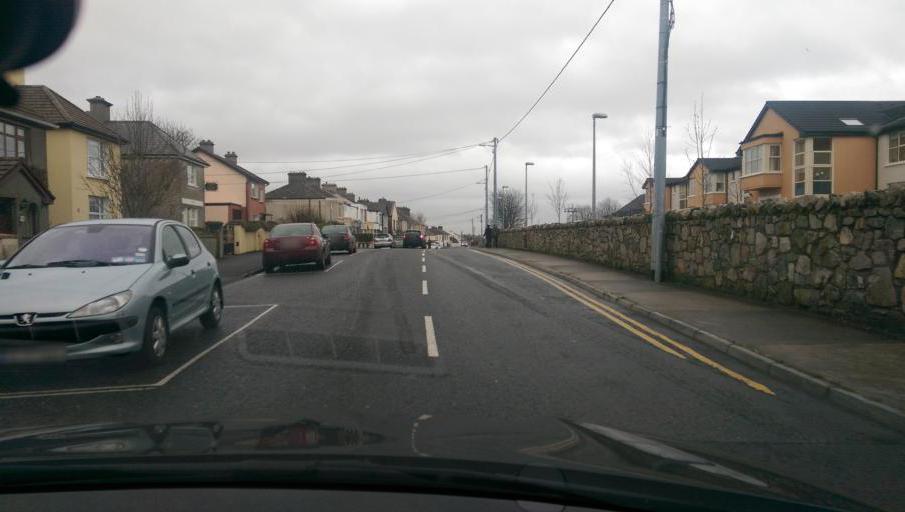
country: IE
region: Connaught
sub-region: County Galway
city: Gaillimh
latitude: 53.2728
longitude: -9.0682
